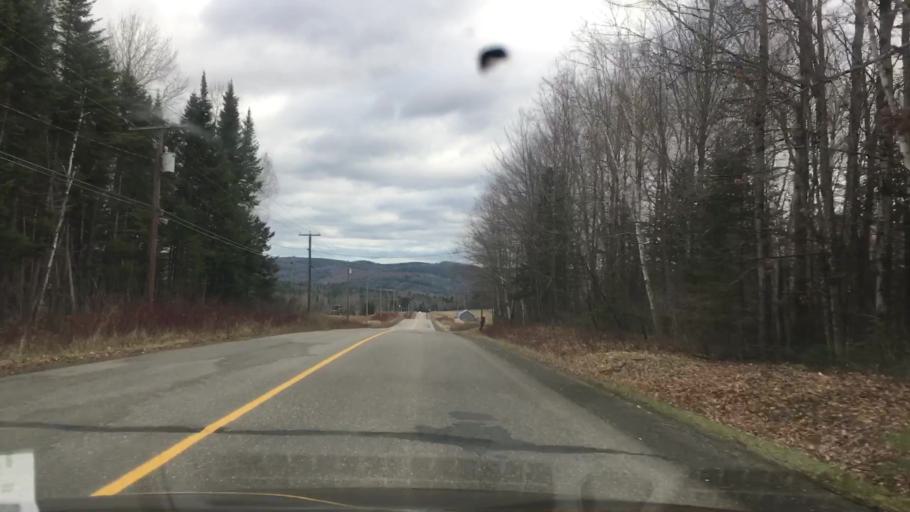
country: US
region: Maine
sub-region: Aroostook County
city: Fort Fairfield
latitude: 46.7482
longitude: -67.7438
